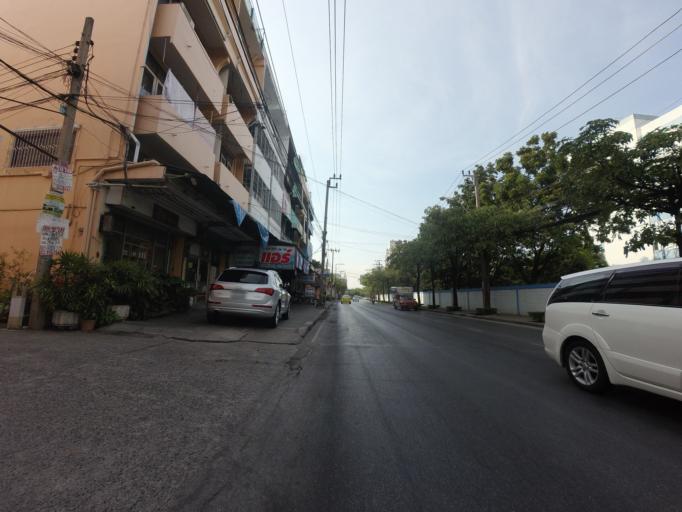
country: TH
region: Bangkok
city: Bang Kapi
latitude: 13.7525
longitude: 100.6168
